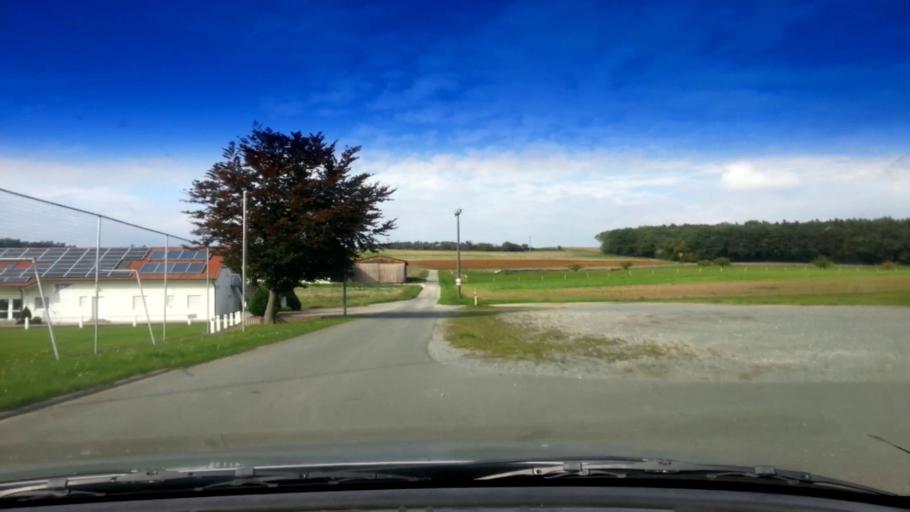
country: DE
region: Bavaria
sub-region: Upper Franconia
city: Gundelsheim
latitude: 49.9683
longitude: 10.9296
